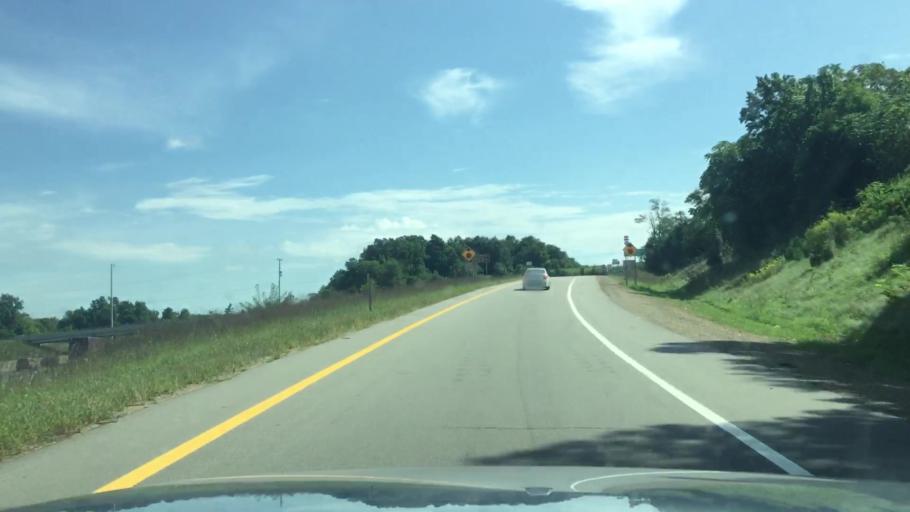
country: US
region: Michigan
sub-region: Kalamazoo County
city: Galesburg
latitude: 42.2728
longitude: -85.4315
